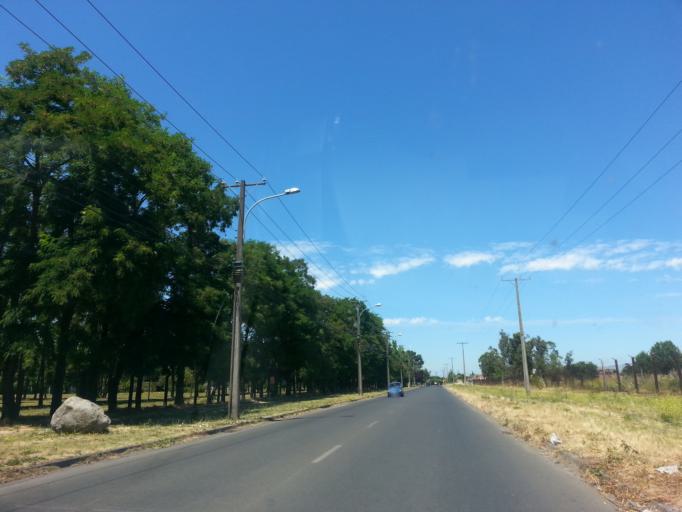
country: CL
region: Biobio
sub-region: Provincia de Nuble
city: Chillan
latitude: -36.6004
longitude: -72.0769
